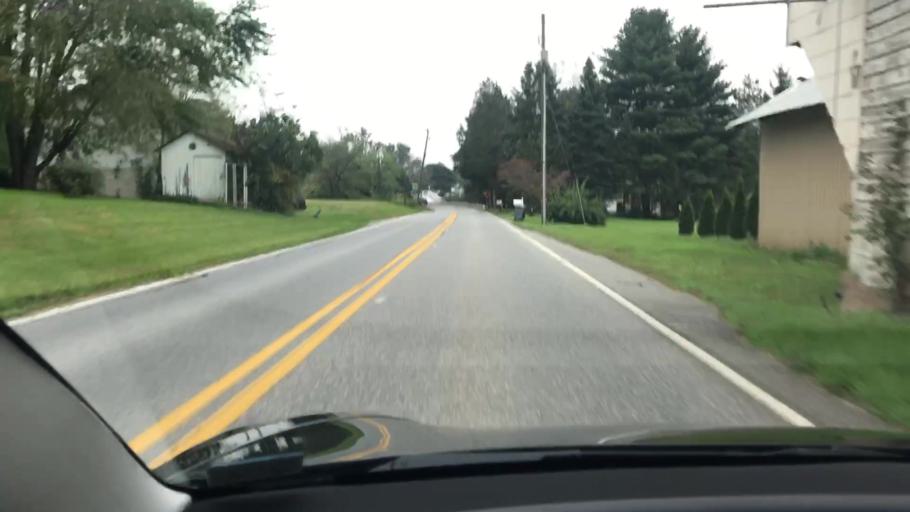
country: US
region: Pennsylvania
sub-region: Cumberland County
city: Lower Allen
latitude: 40.1590
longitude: -76.8871
